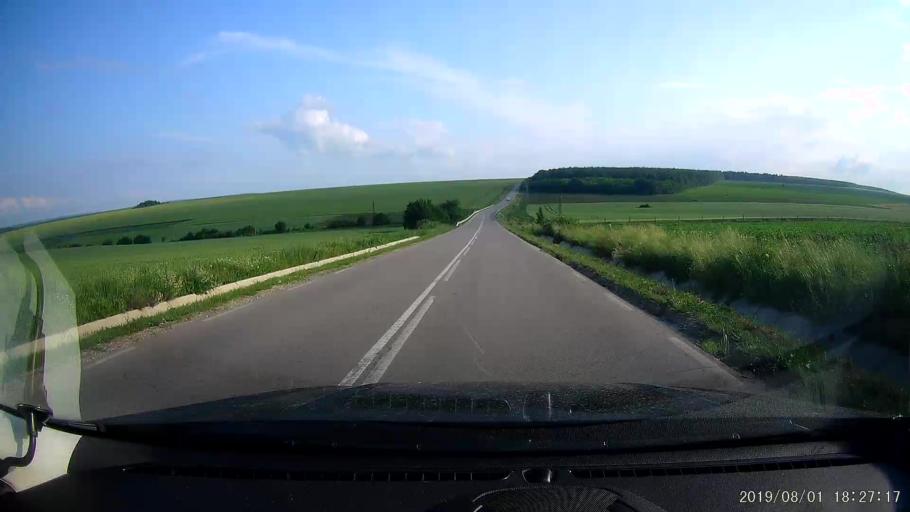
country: BG
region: Shumen
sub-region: Obshtina Venets
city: Venets
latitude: 43.5897
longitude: 26.9833
